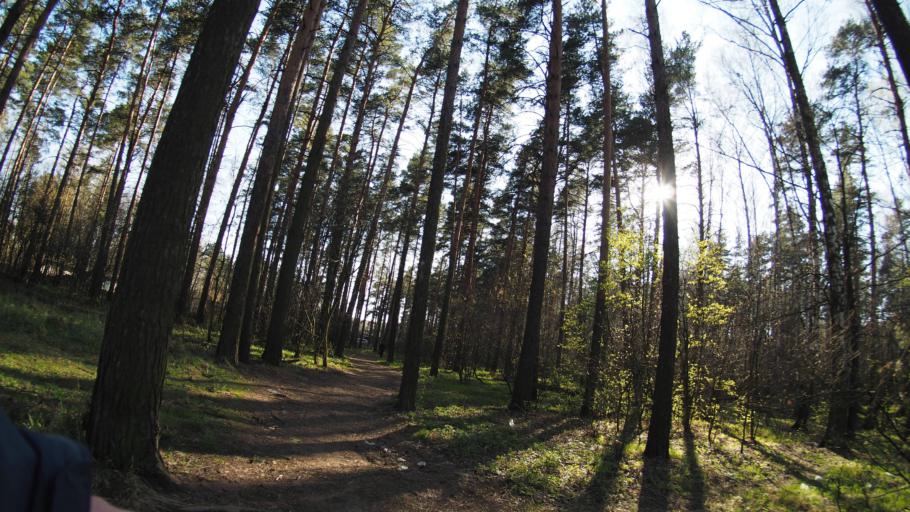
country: RU
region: Moskovskaya
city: Malyshevo
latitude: 55.5143
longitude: 38.3371
